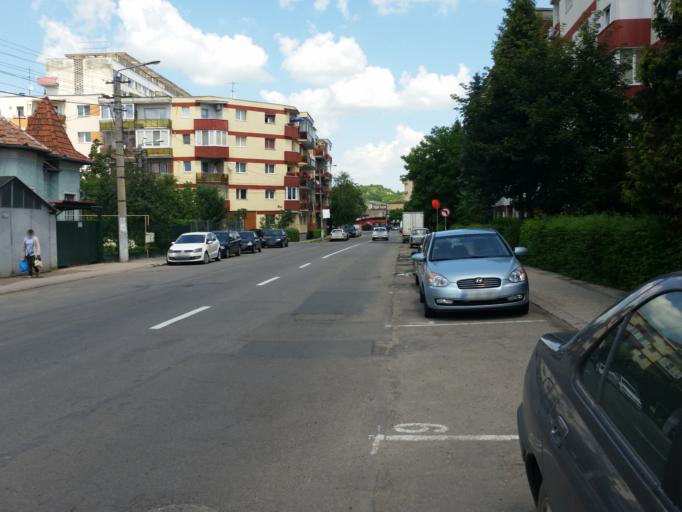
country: RO
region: Cluj
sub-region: Municipiul Cluj-Napoca
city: Cluj-Napoca
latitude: 46.7685
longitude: 23.5530
